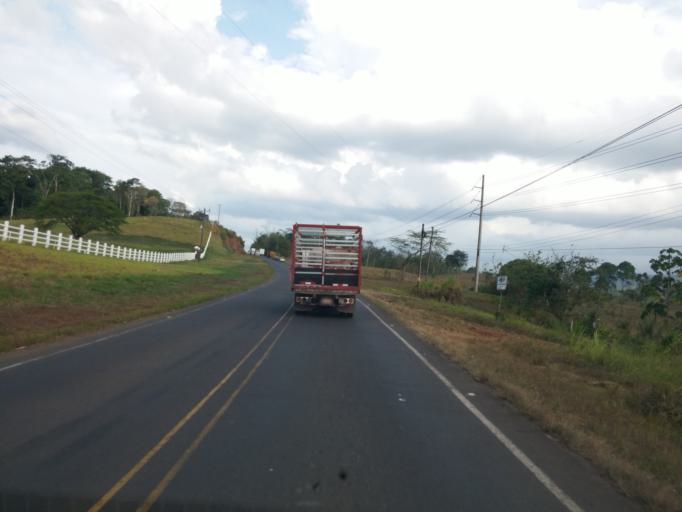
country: CR
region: Alajuela
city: Quesada
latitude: 10.4603
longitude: -84.4214
